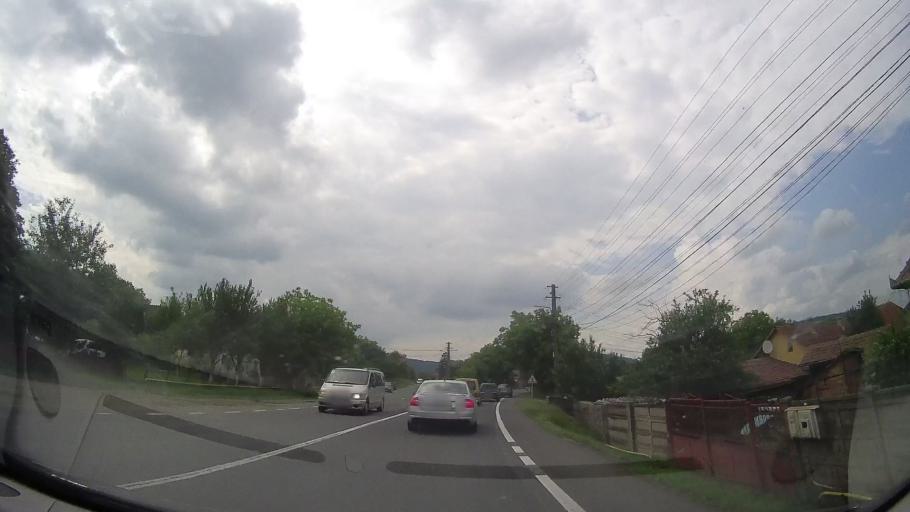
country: RO
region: Hunedoara
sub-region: Comuna Vetel
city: Vetel
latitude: 45.9162
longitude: 22.8508
